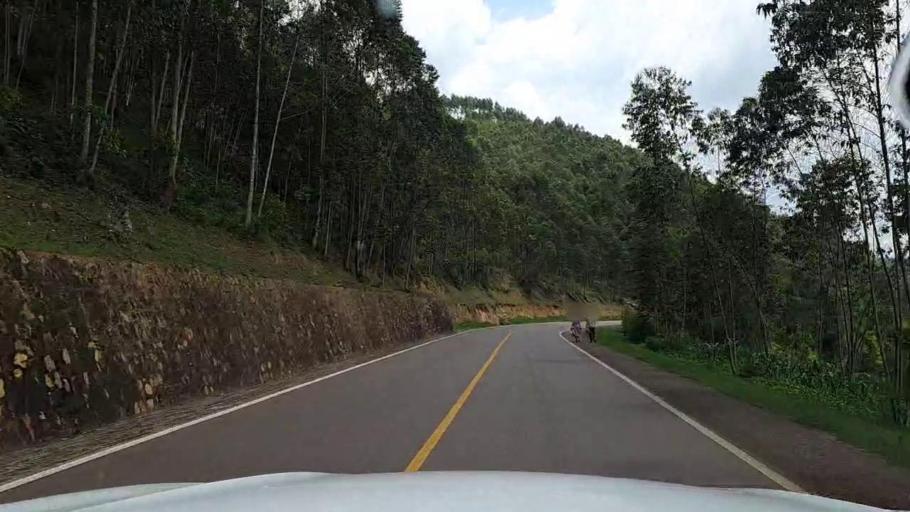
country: RW
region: Kigali
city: Kigali
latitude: -1.8217
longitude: 30.0837
